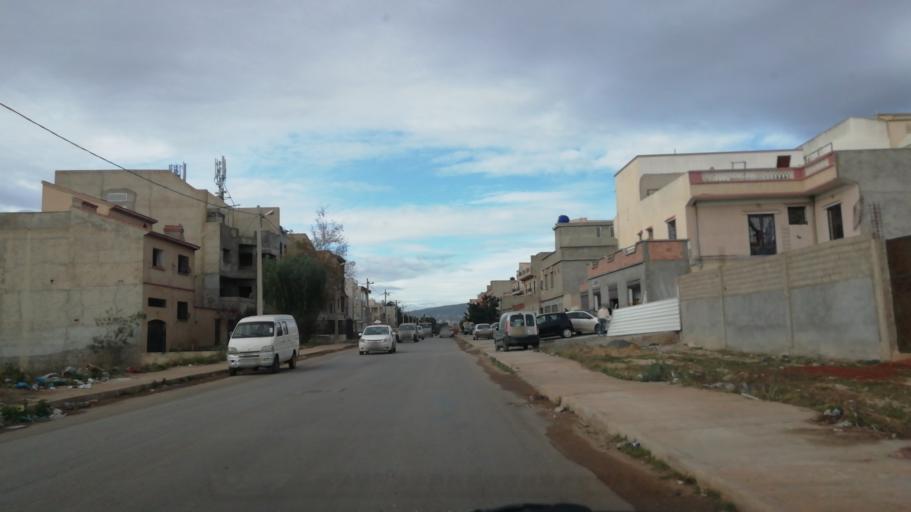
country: DZ
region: Oran
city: Oran
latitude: 35.6920
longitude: -0.6003
